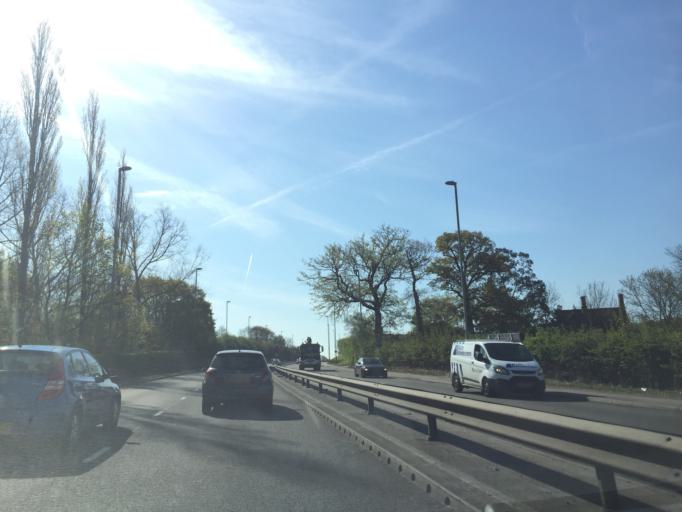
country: GB
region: England
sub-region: Essex
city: Harlow
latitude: 51.7536
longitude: 0.1305
